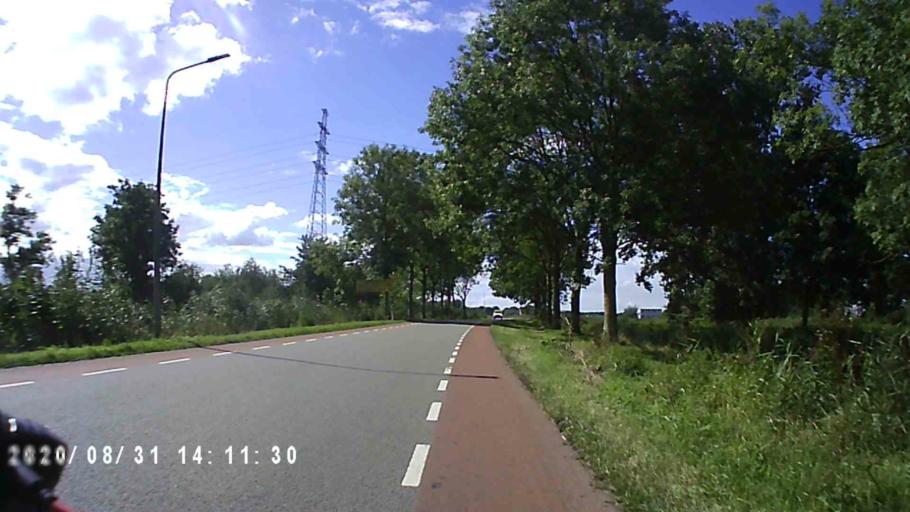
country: NL
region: Groningen
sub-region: Gemeente Zuidhorn
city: Aduard
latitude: 53.2104
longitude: 6.4788
